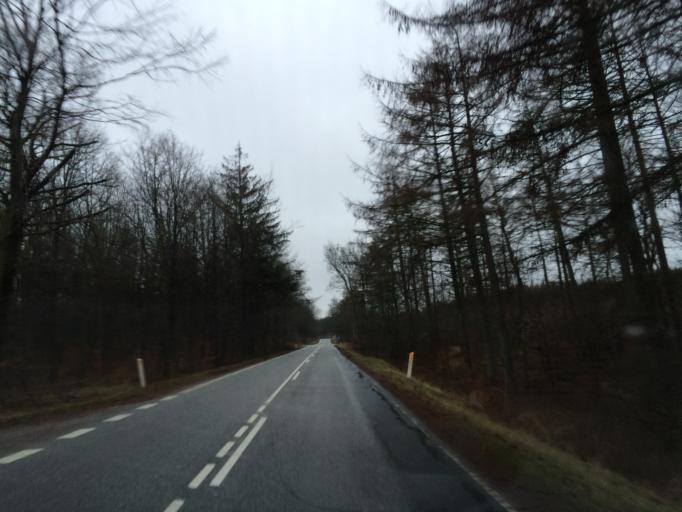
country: DK
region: North Denmark
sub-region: Rebild Kommune
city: Stovring
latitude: 56.8241
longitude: 9.8192
